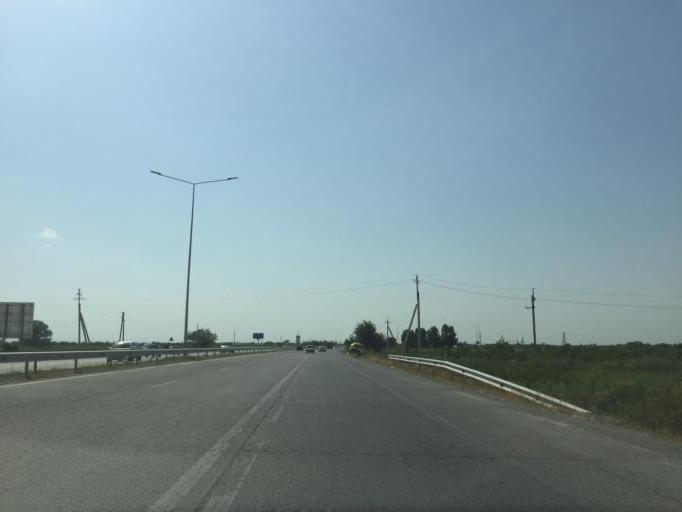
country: AM
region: Ararat
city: Mrgavan
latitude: 39.9581
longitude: 44.5261
